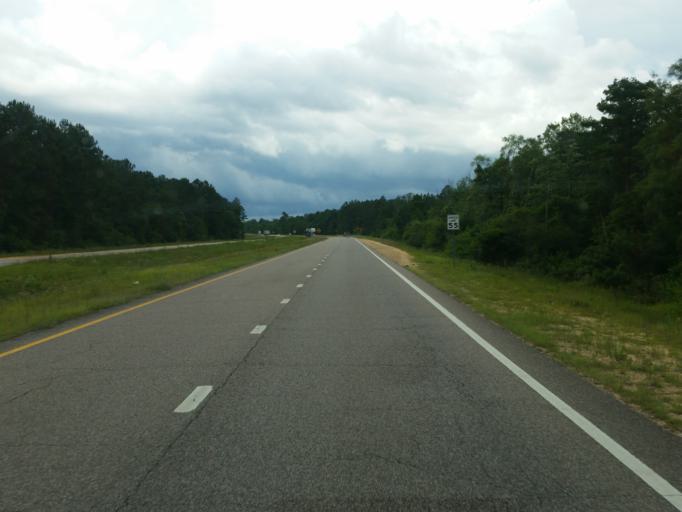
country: US
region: Mississippi
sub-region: George County
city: Lucedale
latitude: 30.8687
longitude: -88.4260
